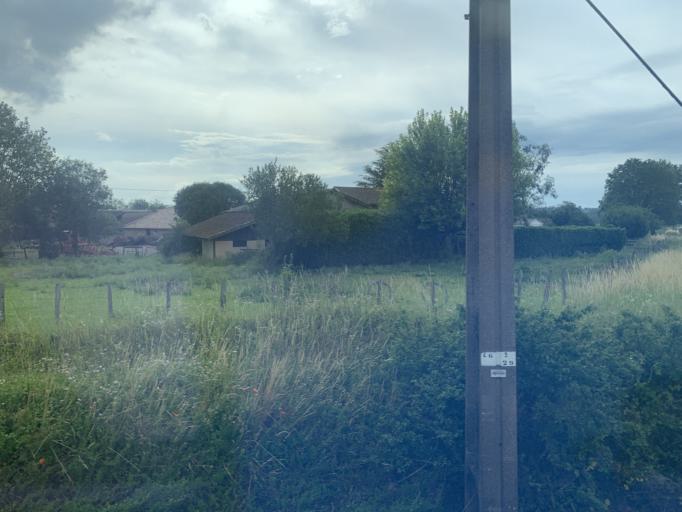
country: FR
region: Rhone-Alpes
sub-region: Departement du Rhone
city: Belleville
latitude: 46.1012
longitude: 4.7267
